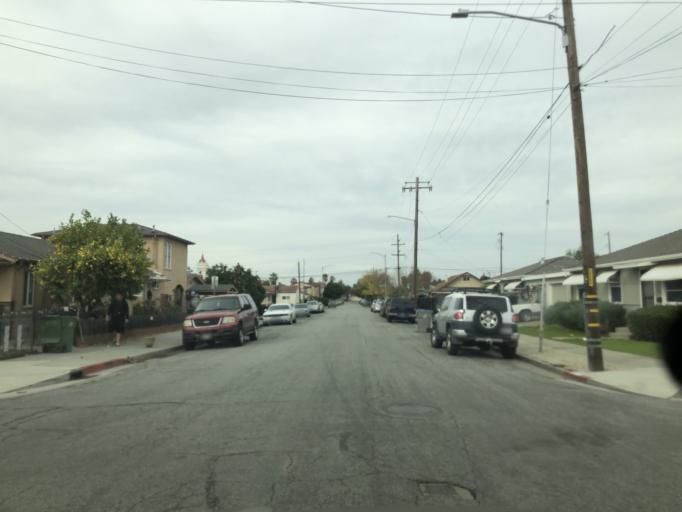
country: US
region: California
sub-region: Santa Clara County
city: San Jose
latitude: 37.3471
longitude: -121.8607
